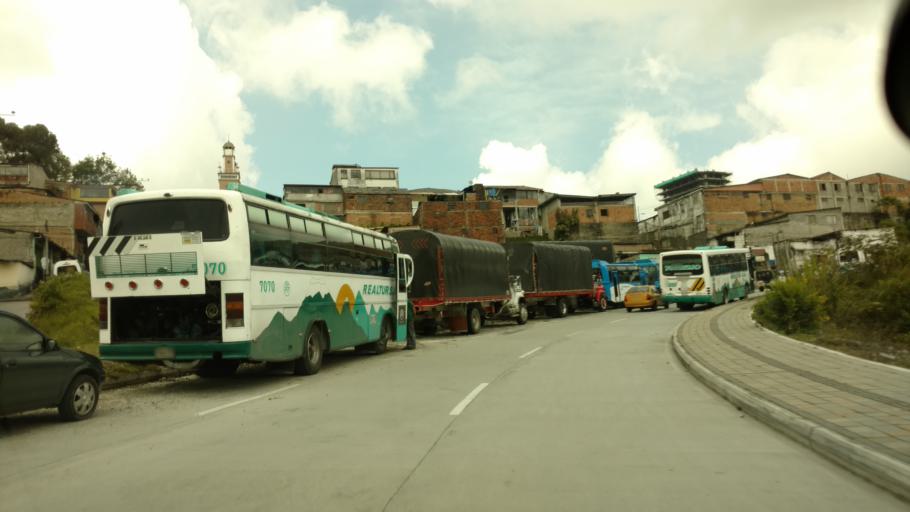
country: CO
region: Caldas
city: Manizales
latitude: 5.0744
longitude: -75.5174
